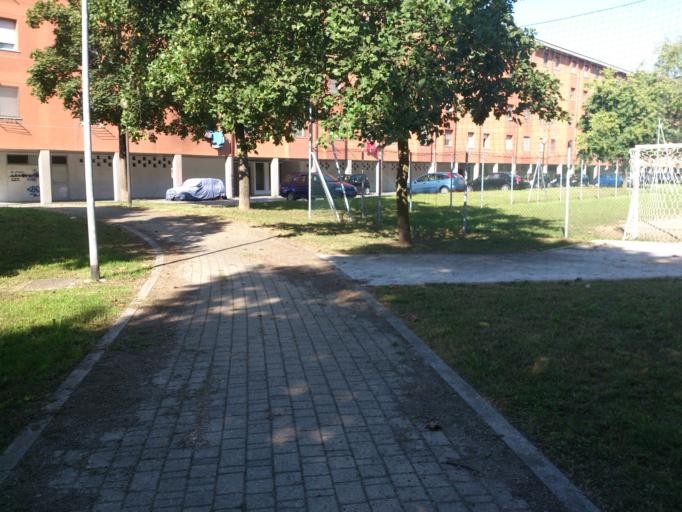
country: IT
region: Lombardy
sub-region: Citta metropolitana di Milano
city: San Donato Milanese
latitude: 45.4198
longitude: 9.2647
